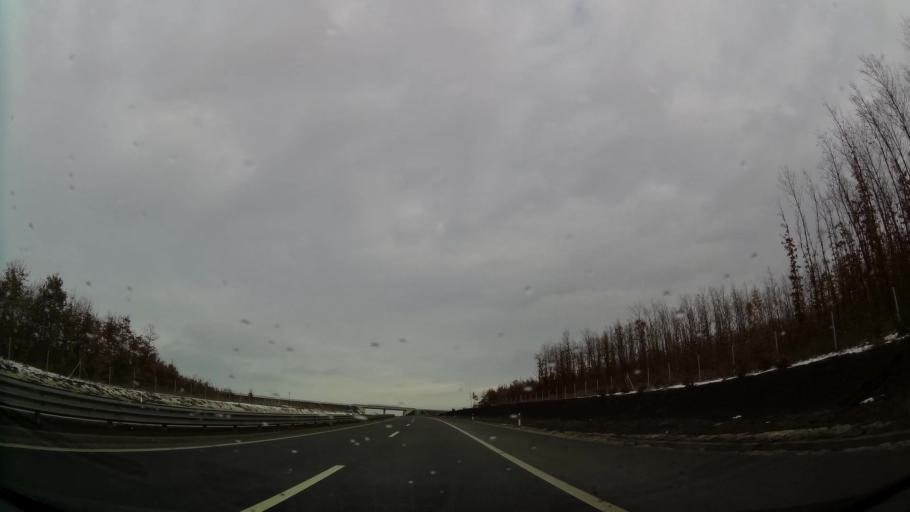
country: XK
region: Ferizaj
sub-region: Komuna e Ferizajt
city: Ferizaj
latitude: 42.3470
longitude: 21.2056
